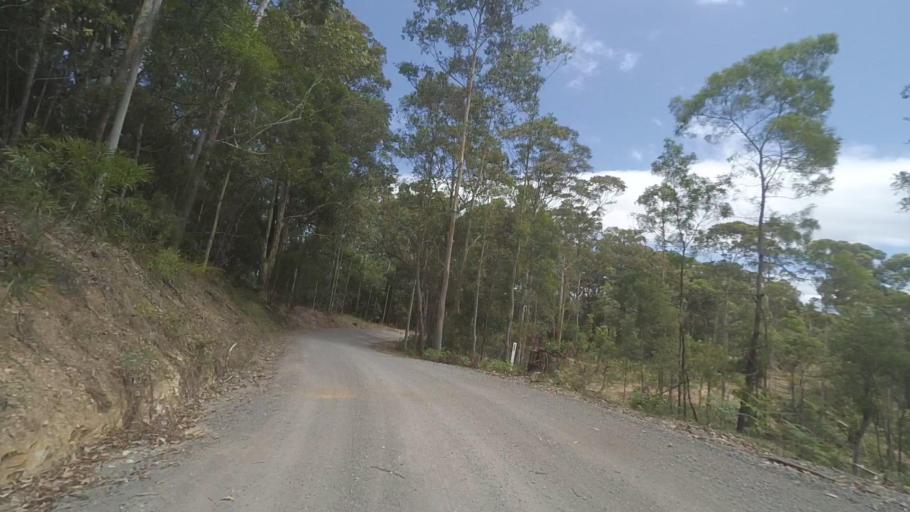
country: AU
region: New South Wales
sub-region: Shoalhaven Shire
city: Milton
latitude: -35.4422
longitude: 150.2959
